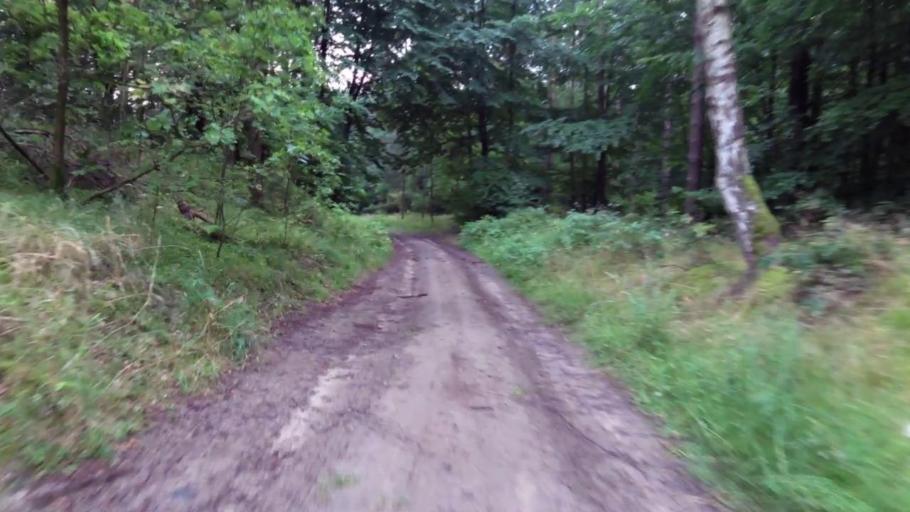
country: PL
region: West Pomeranian Voivodeship
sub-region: Powiat szczecinecki
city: Lubowo
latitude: 53.5989
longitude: 16.3845
